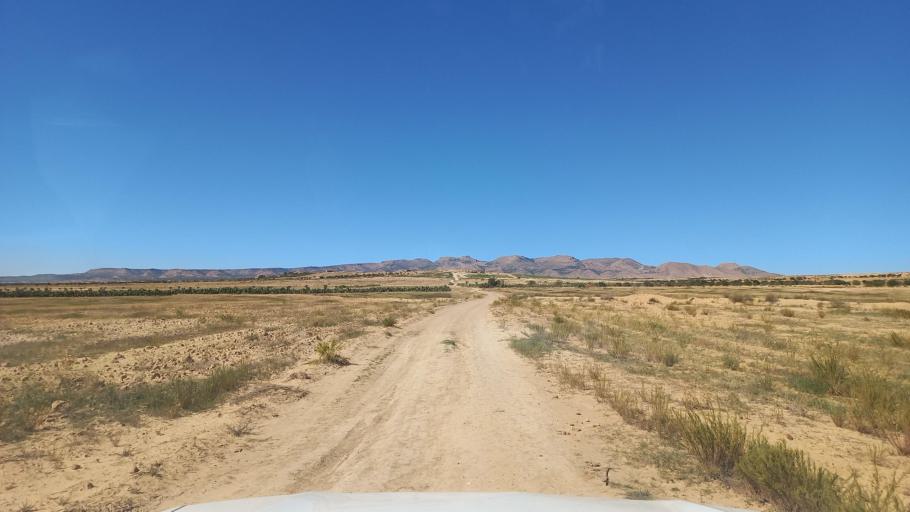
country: TN
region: Al Qasrayn
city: Sbiba
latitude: 35.3697
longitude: 9.0846
